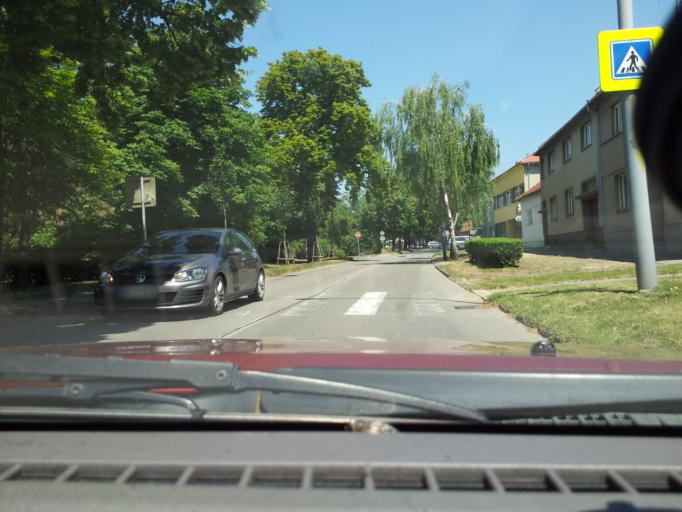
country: CZ
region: South Moravian
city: Sokolnice
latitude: 49.1451
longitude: 16.6655
